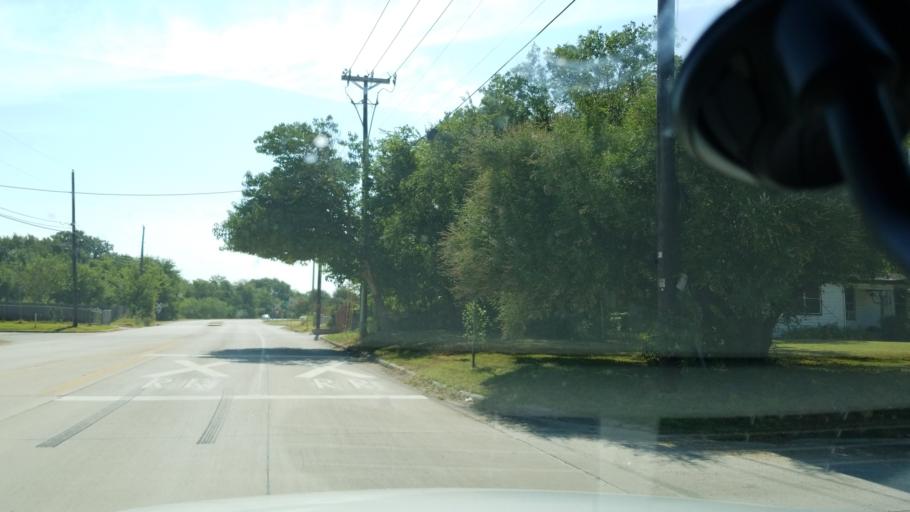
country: US
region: Texas
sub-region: Dallas County
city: Grand Prairie
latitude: 32.7602
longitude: -96.9570
